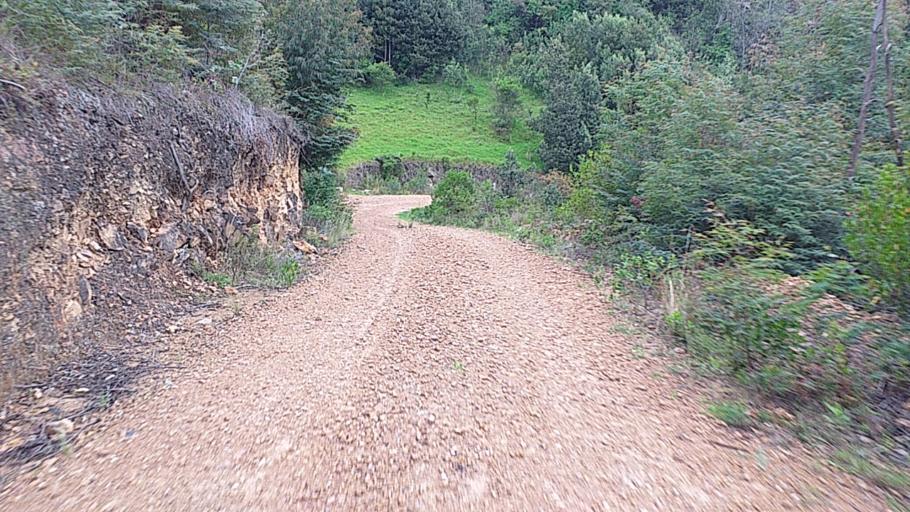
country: CO
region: Boyaca
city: Floresta
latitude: 5.8853
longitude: -72.9098
